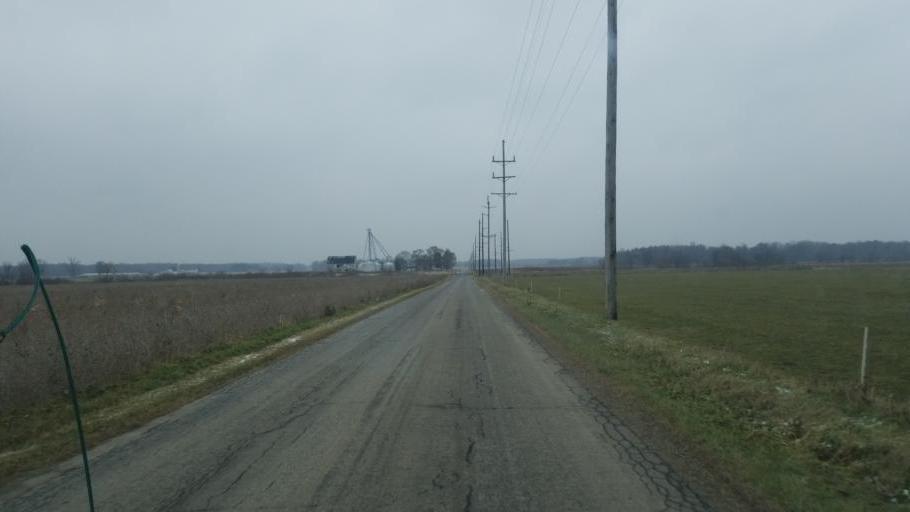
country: US
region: Ohio
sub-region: Richland County
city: Shelby
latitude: 40.9139
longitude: -82.6859
